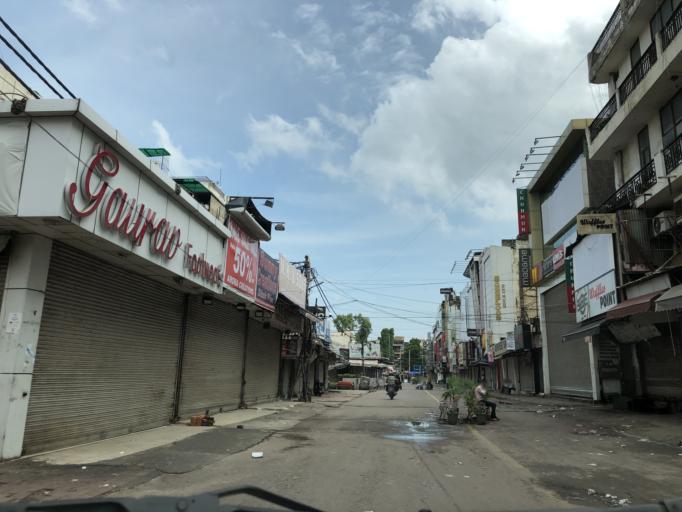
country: IN
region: NCT
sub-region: New Delhi
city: New Delhi
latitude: 28.5684
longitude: 77.2421
